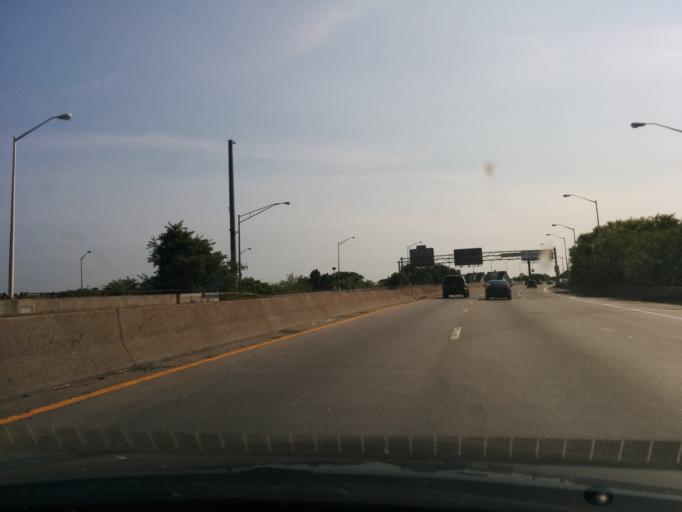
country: US
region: New York
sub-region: Queens County
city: Long Island City
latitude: 40.7345
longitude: -73.9219
